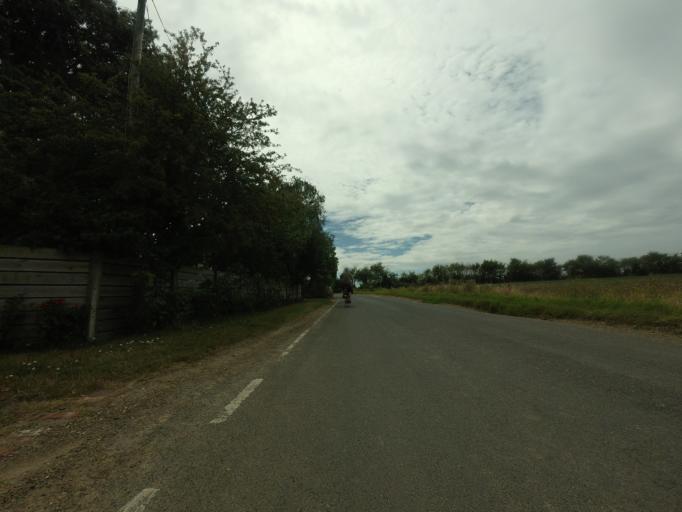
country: GB
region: England
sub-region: Medway
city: Stoke
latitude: 51.4394
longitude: 0.5989
